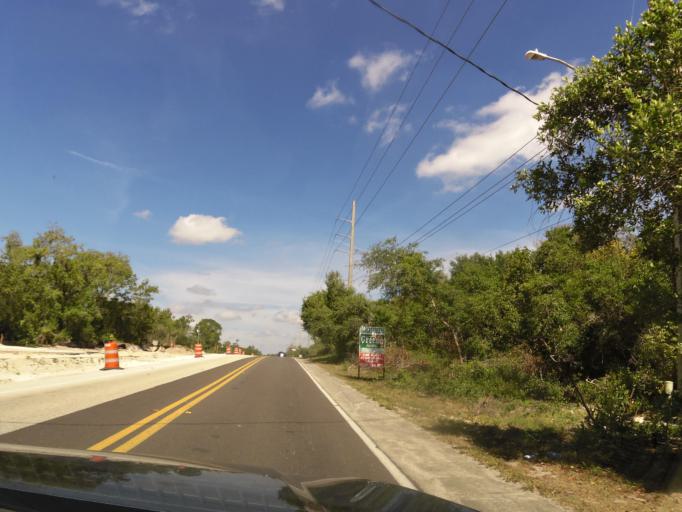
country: US
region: Florida
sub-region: Volusia County
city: Lake Helen
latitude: 28.9303
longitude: -81.1979
